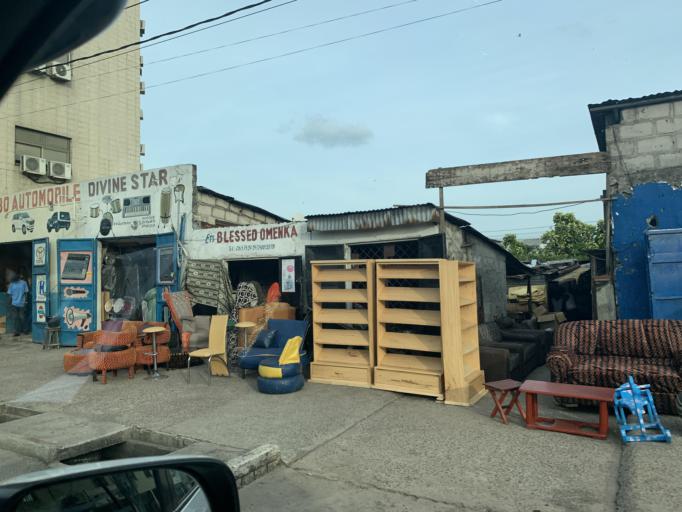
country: CG
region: Brazzaville
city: Brazzaville
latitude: -4.2480
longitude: 15.2813
